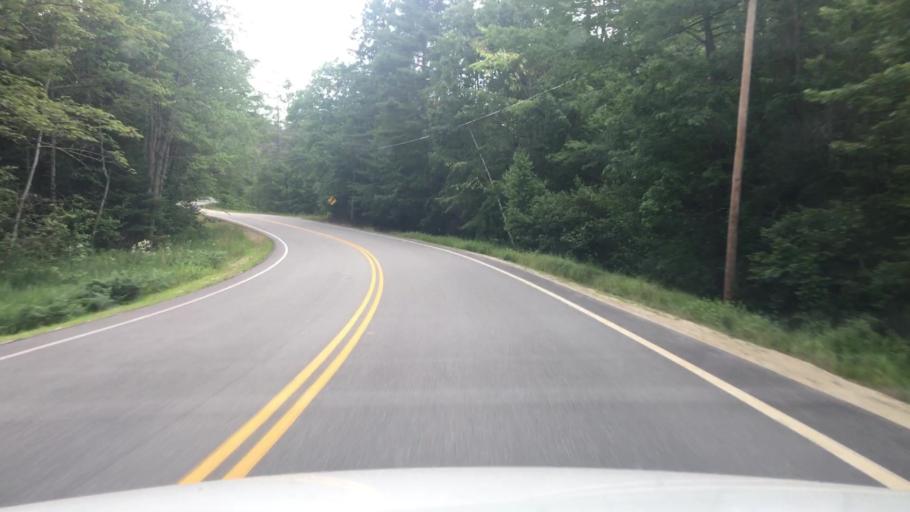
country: US
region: Maine
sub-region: Oxford County
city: Hartford
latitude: 44.3763
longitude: -70.4087
